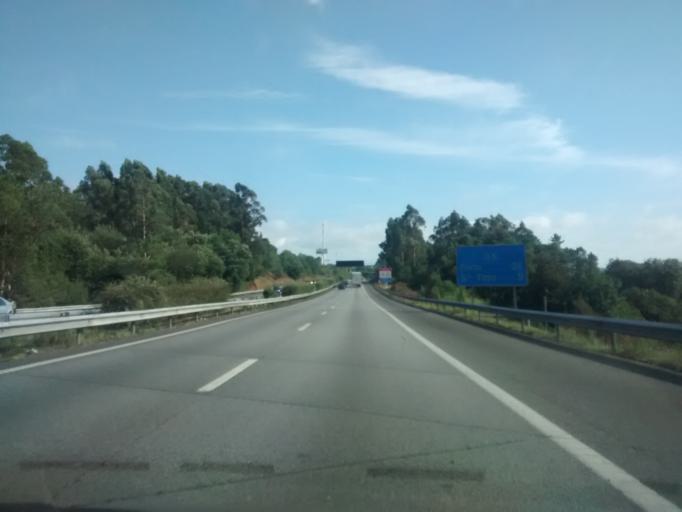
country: PT
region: Porto
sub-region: Santo Tirso
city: Santo Tirso
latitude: 41.3678
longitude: -8.5024
